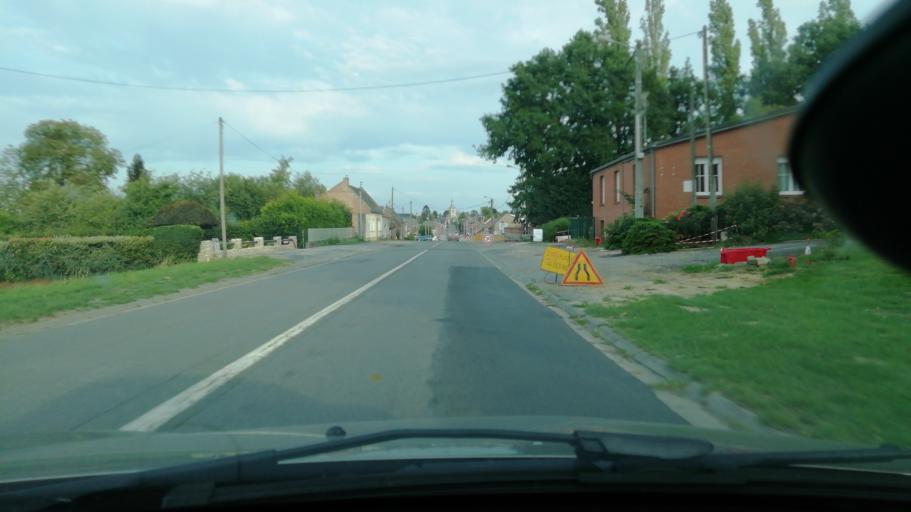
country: FR
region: Nord-Pas-de-Calais
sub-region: Departement du Nord
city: Viesly
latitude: 50.1254
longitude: 3.4493
